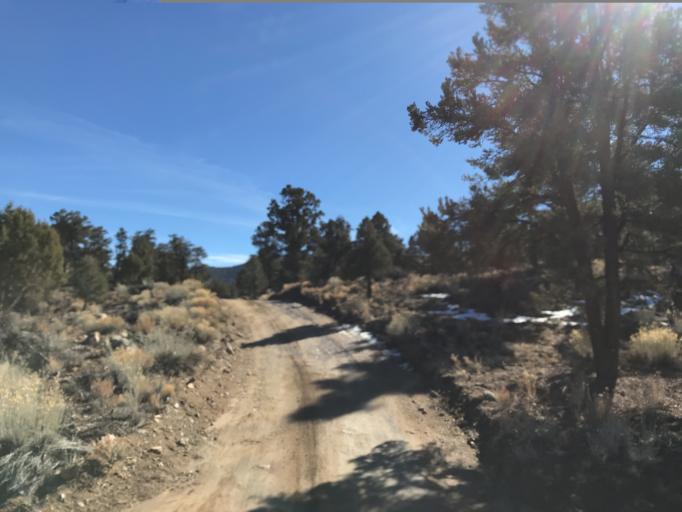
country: US
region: California
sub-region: San Bernardino County
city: Big Bear City
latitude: 34.2586
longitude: -116.7504
